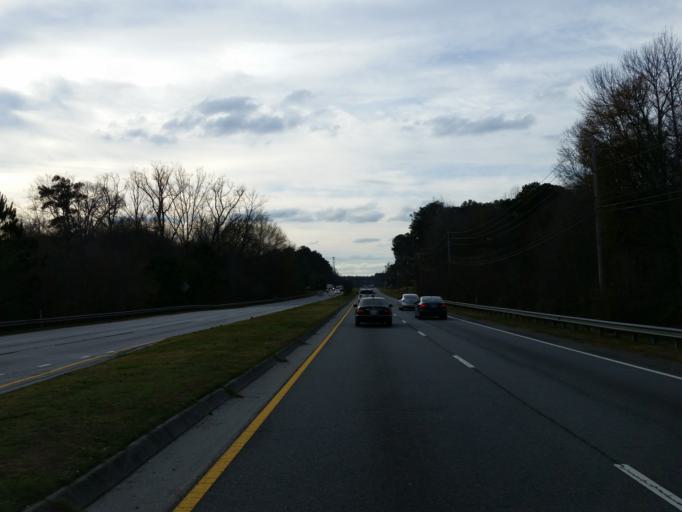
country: US
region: Georgia
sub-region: Cobb County
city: Powder Springs
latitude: 33.8997
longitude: -84.6291
